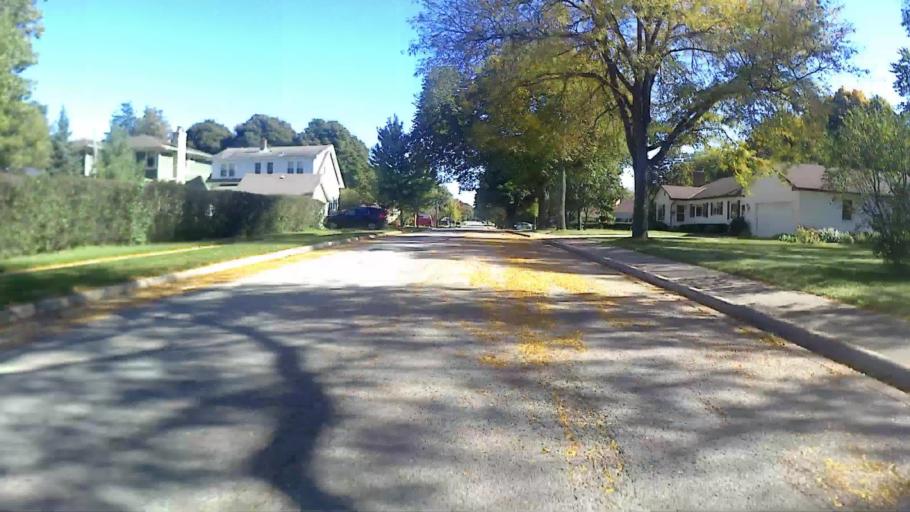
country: US
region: Illinois
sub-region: DuPage County
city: Itasca
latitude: 41.9659
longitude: -88.0153
